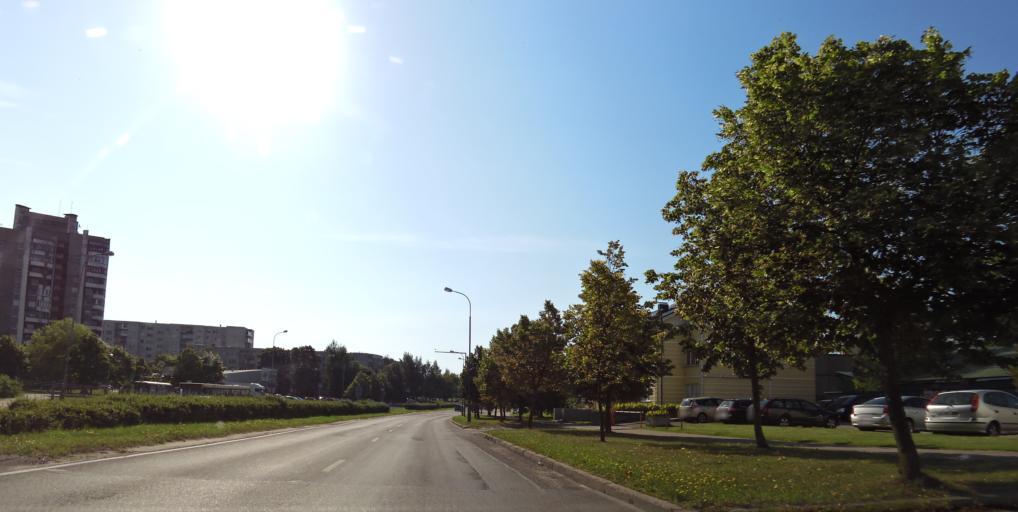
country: LT
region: Vilnius County
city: Seskine
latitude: 54.7141
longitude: 25.2364
